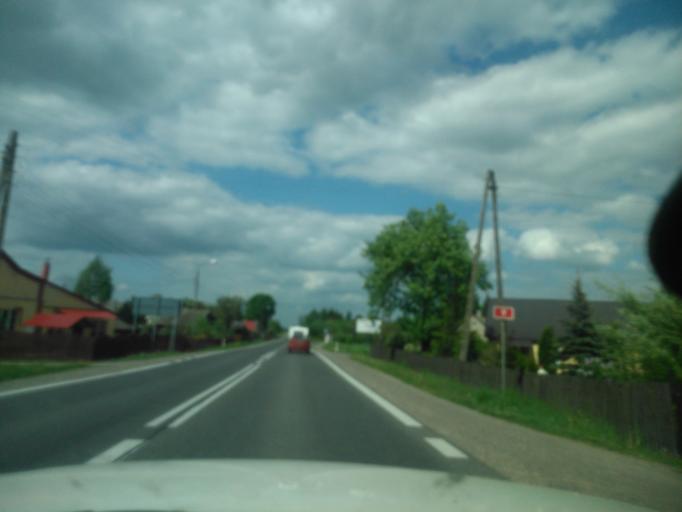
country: PL
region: Masovian Voivodeship
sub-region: Powiat radomski
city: Ilza
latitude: 51.1179
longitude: 21.2234
